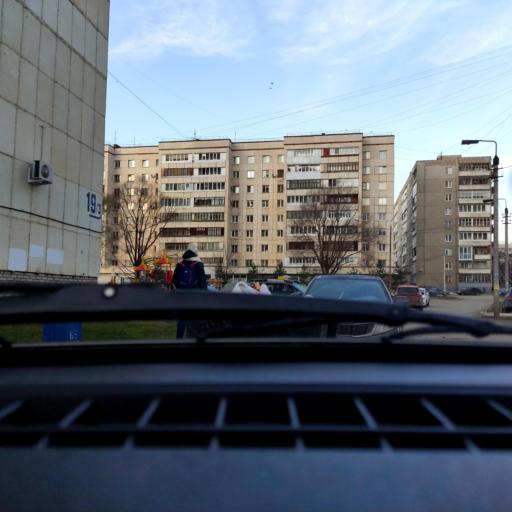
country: RU
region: Bashkortostan
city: Ufa
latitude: 54.7818
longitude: 56.1348
